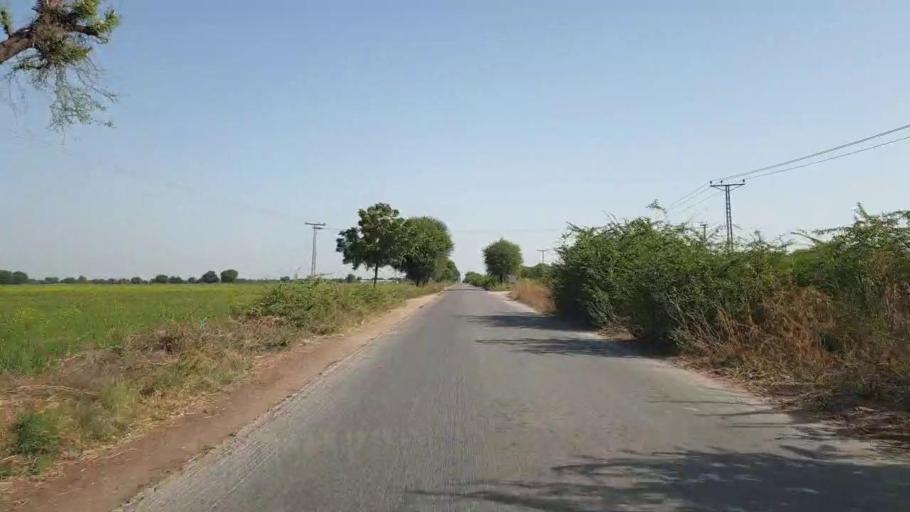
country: PK
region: Sindh
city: Chor
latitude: 25.4420
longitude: 69.7505
